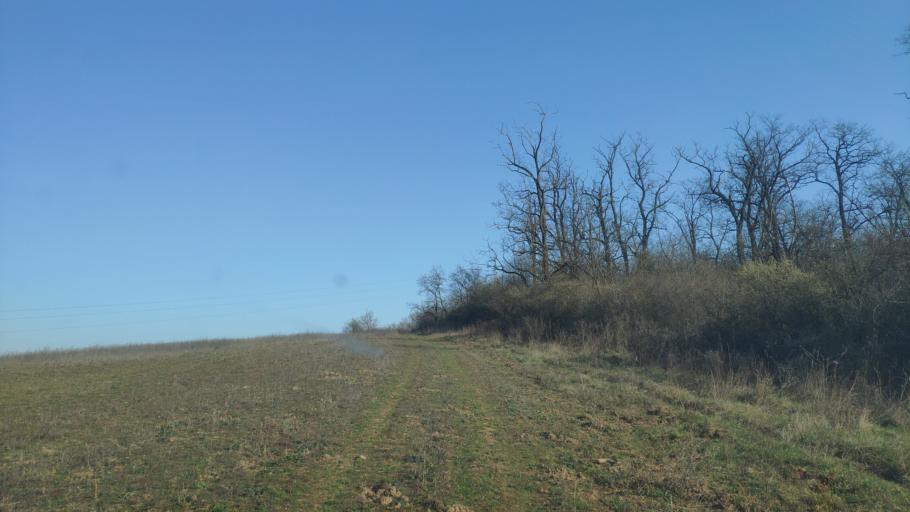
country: SK
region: Banskobystricky
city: Revuca
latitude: 48.5497
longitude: 20.2505
